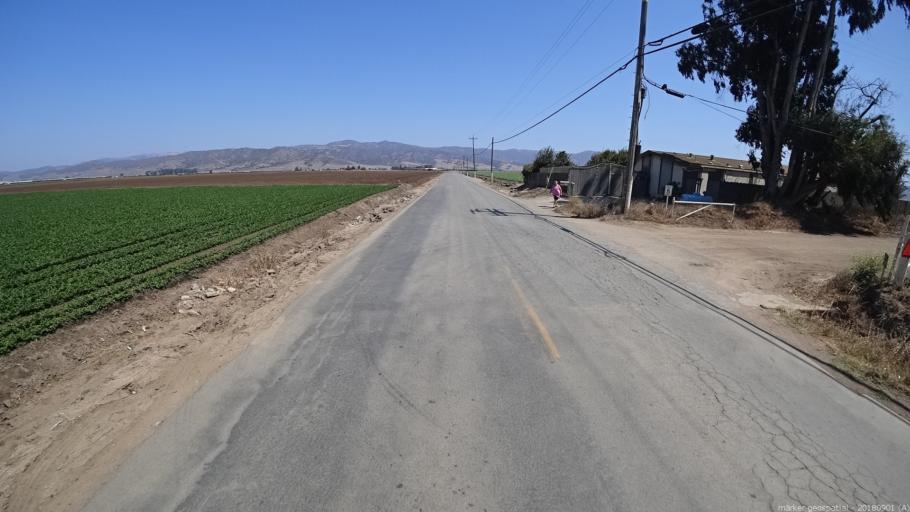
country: US
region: California
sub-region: Monterey County
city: Chualar
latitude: 36.6165
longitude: -121.5410
